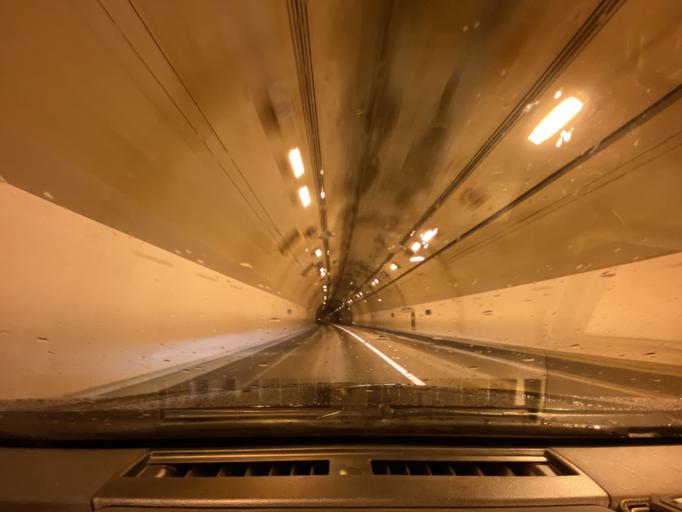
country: JP
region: Hokkaido
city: Rumoi
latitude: 43.6882
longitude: 141.3405
